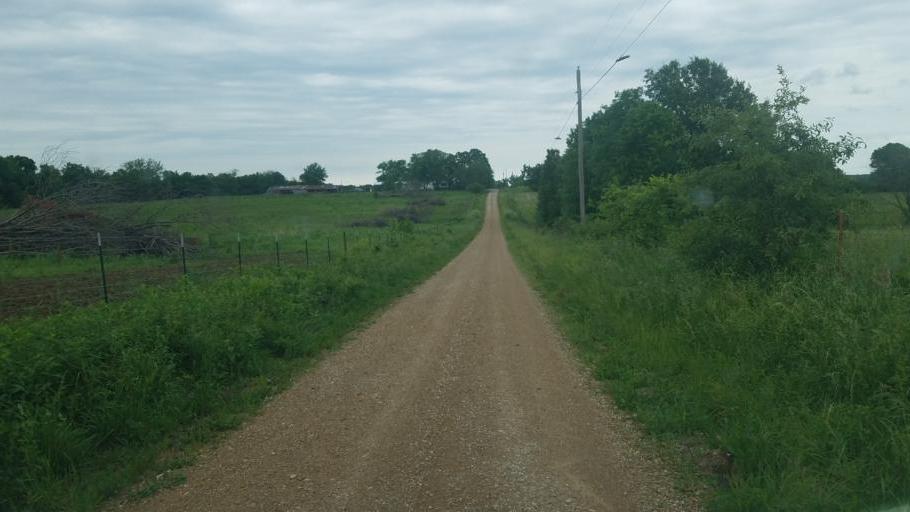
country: US
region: Missouri
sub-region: Moniteau County
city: California
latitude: 38.6021
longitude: -92.6474
